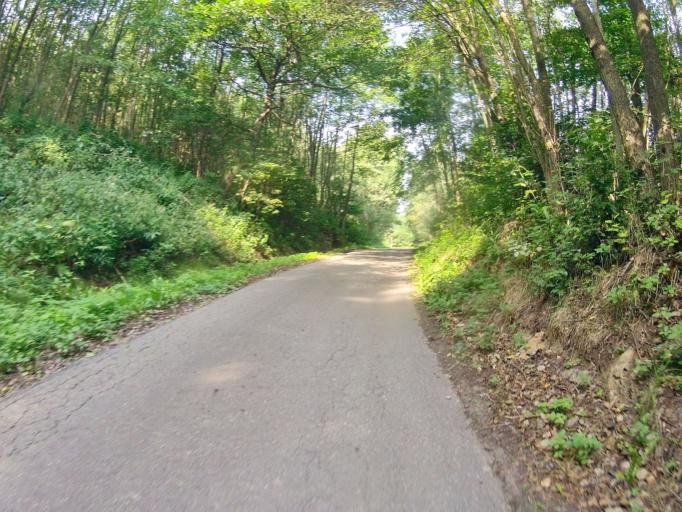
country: PL
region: Subcarpathian Voivodeship
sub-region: Powiat jasielski
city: Brzyska
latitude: 49.7954
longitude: 21.3720
